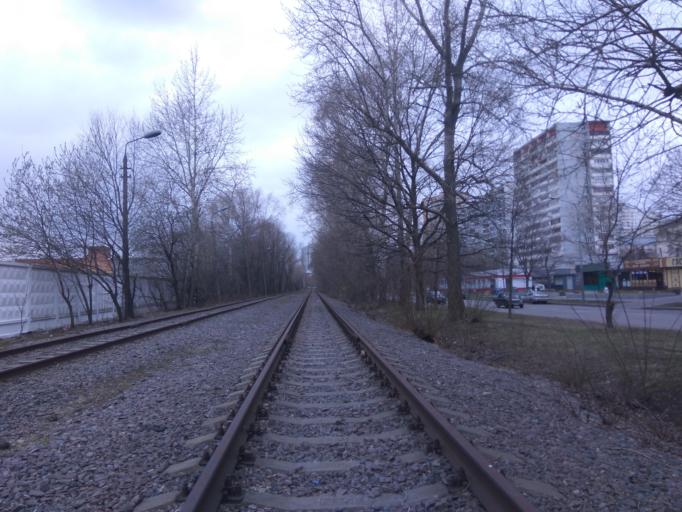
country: RU
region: Moscow
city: Vagonoremont
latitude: 55.9006
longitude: 37.5535
